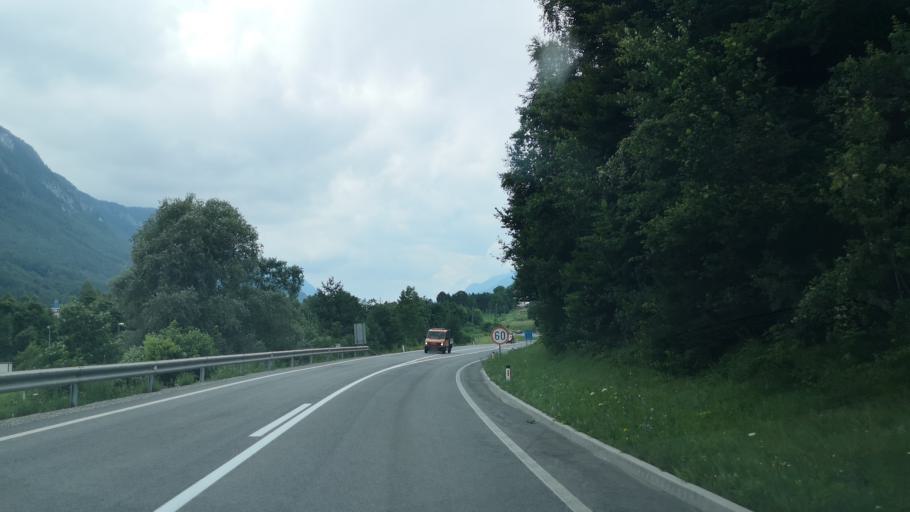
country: SI
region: Jesenice
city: Hrusica
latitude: 46.4451
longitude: 14.0275
